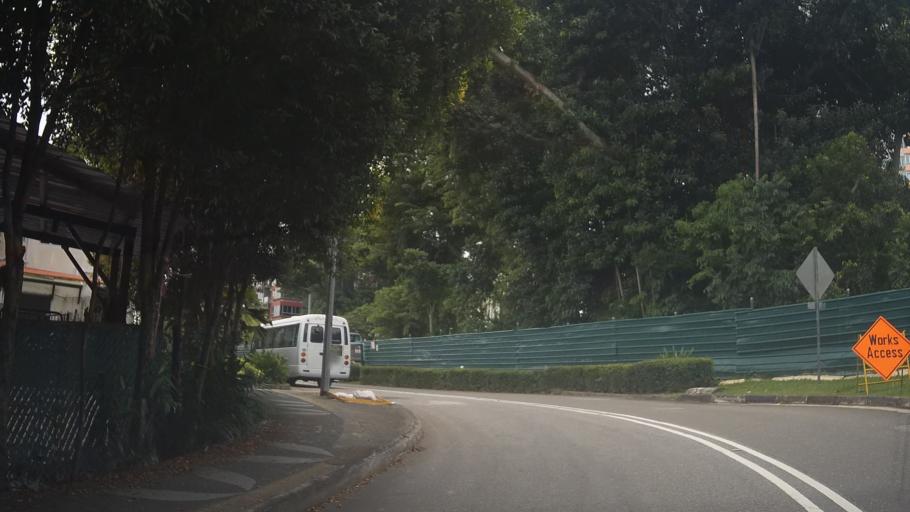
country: SG
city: Singapore
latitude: 1.3409
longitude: 103.7794
